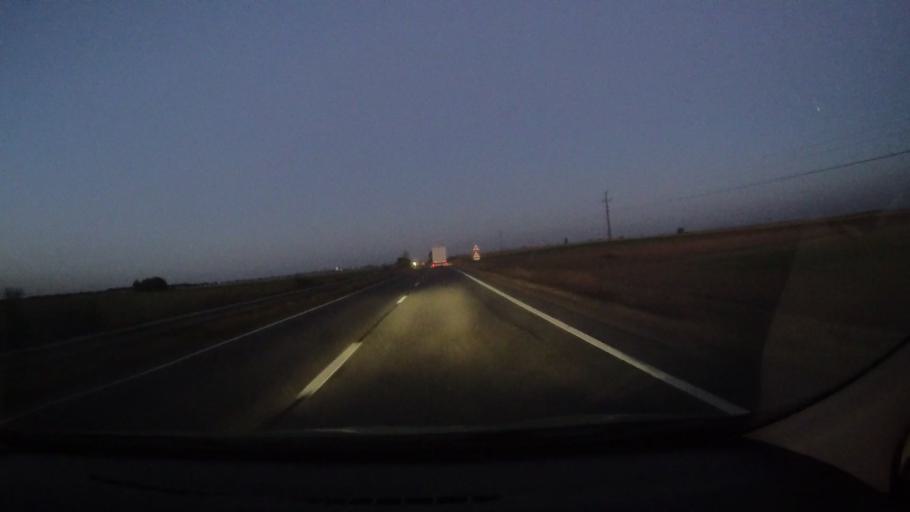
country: RO
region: Bihor
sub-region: Comuna Curtuiuseni
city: Curtuiseni
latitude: 47.5240
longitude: 22.1806
